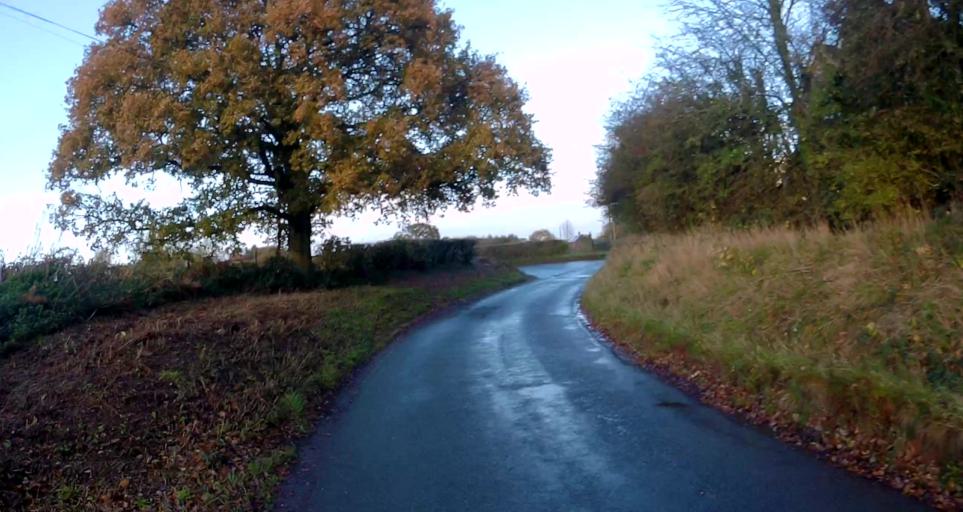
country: GB
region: England
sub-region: Hampshire
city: Basingstoke
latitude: 51.2128
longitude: -1.0902
